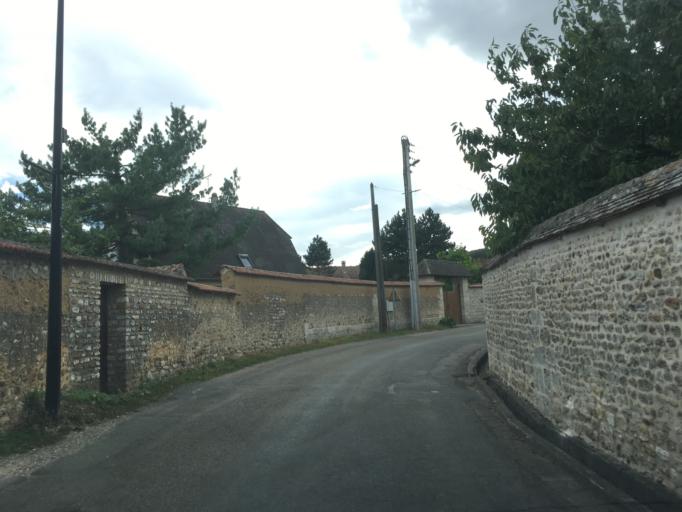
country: FR
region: Haute-Normandie
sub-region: Departement de l'Eure
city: Saint-Just
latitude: 49.1154
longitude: 1.4387
